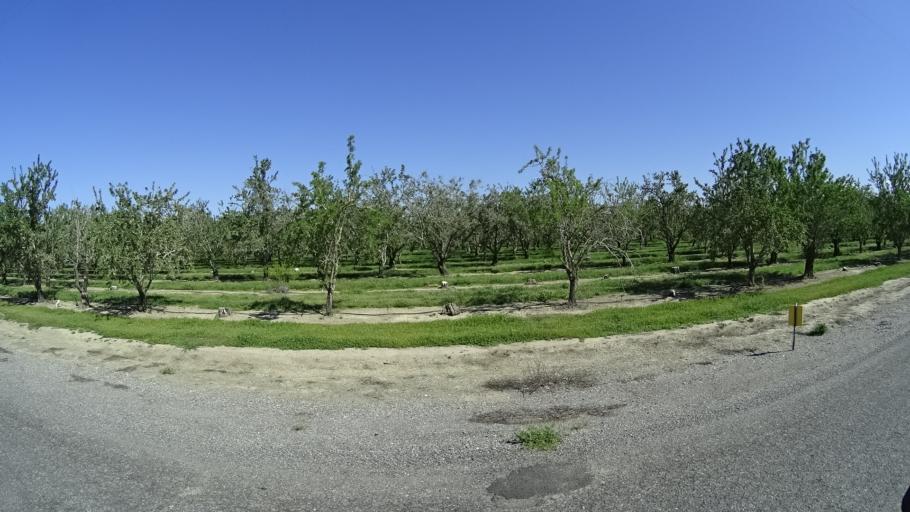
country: US
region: California
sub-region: Glenn County
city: Hamilton City
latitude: 39.7286
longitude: -122.0223
